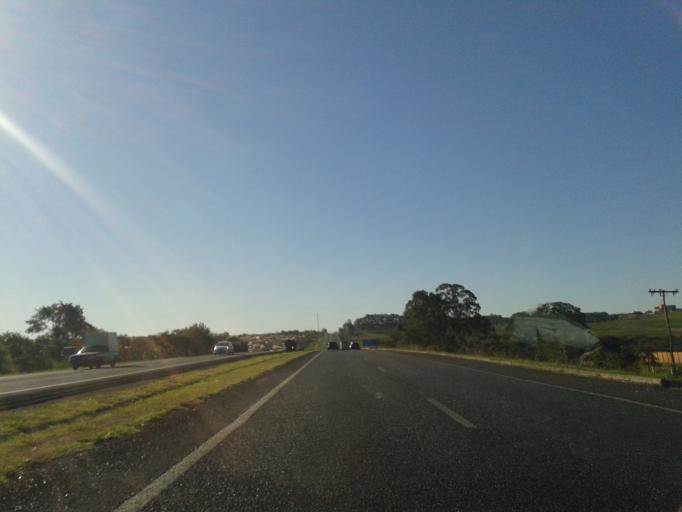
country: BR
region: Minas Gerais
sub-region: Uberlandia
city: Uberlandia
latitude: -18.9622
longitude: -48.2157
